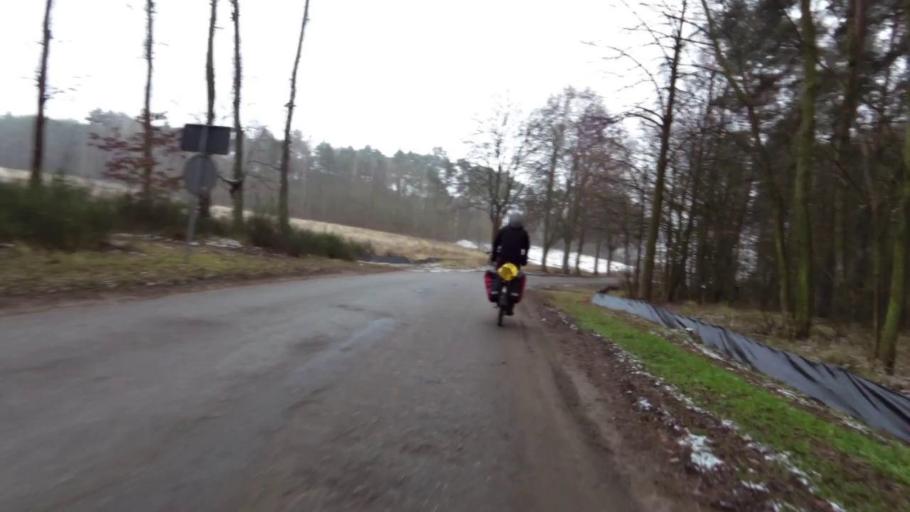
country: PL
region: West Pomeranian Voivodeship
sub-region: Powiat walecki
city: Walcz
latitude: 53.2984
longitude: 16.4776
